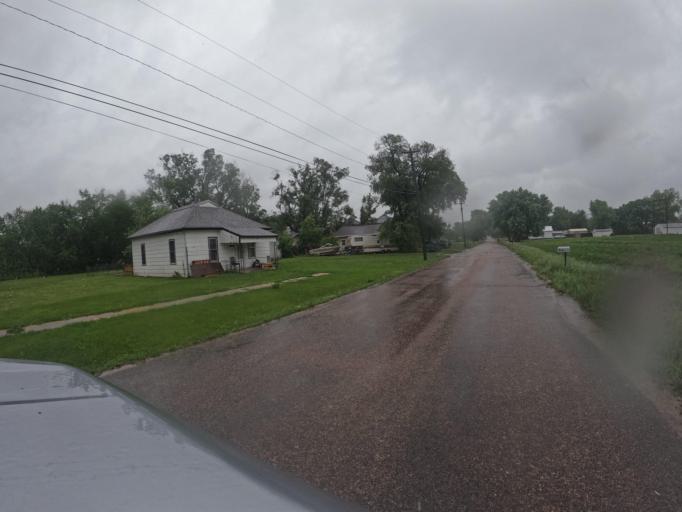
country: US
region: Nebraska
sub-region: Gage County
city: Wymore
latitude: 40.1252
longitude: -96.6593
